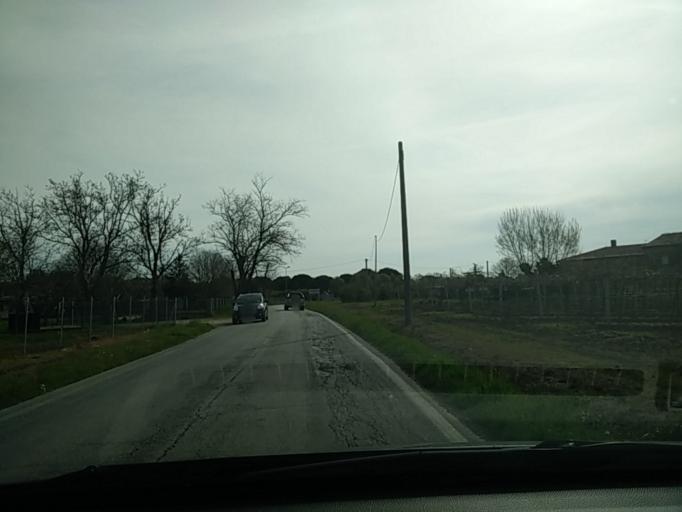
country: IT
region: Emilia-Romagna
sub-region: Provincia di Rimini
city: Santa Giustina
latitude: 44.0815
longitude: 12.4991
